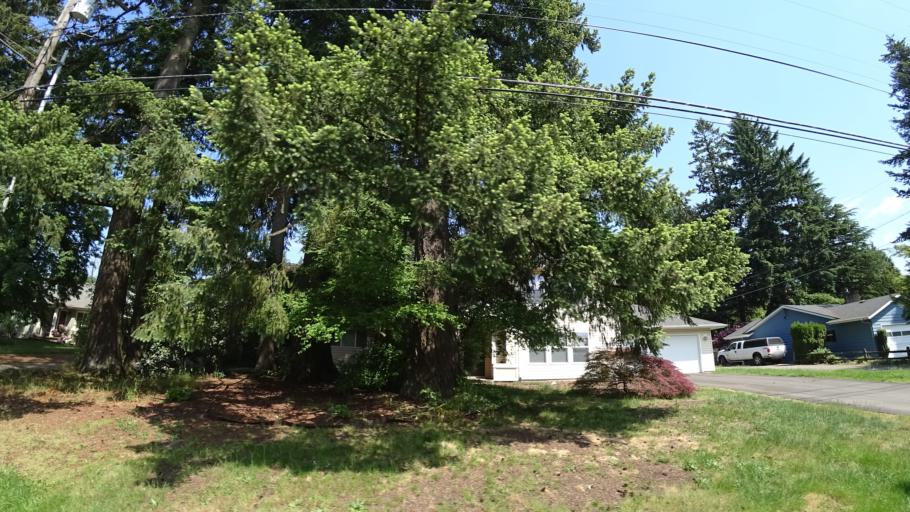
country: US
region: Oregon
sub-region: Washington County
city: Metzger
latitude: 45.4540
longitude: -122.7334
